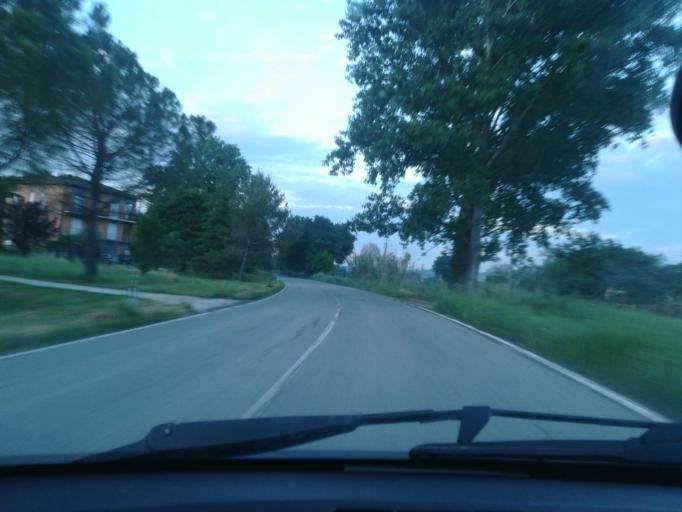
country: IT
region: The Marches
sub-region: Provincia di Macerata
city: Pollenza
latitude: 43.2924
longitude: 13.3682
